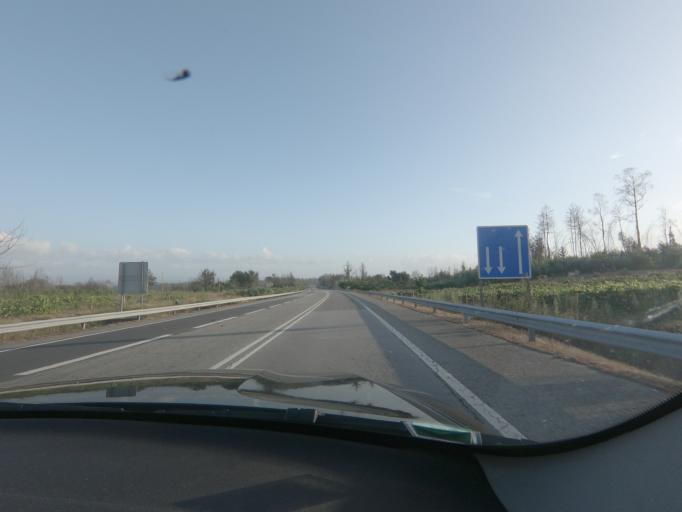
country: PT
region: Viseu
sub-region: Concelho de Tondela
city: Tondela
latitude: 40.4647
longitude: -8.1004
